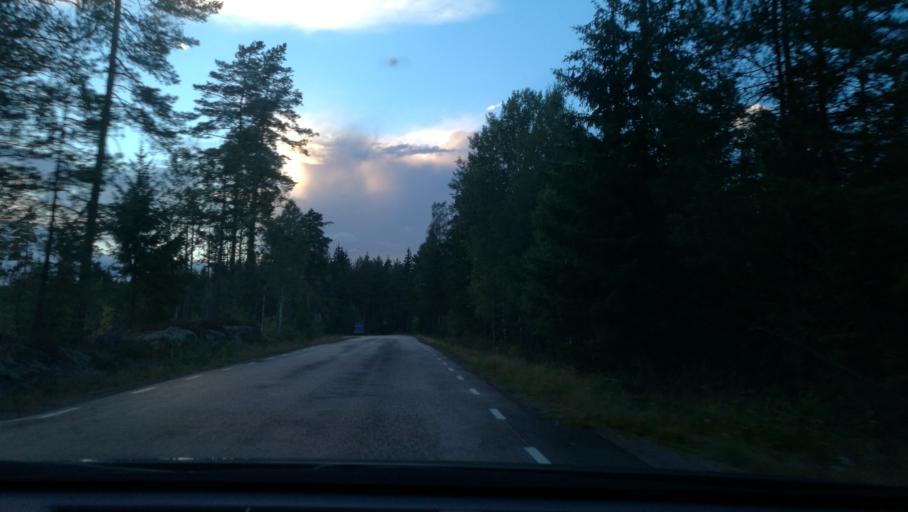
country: SE
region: OEstergoetland
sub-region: Norrkopings Kommun
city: Svartinge
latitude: 58.8185
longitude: 16.0714
